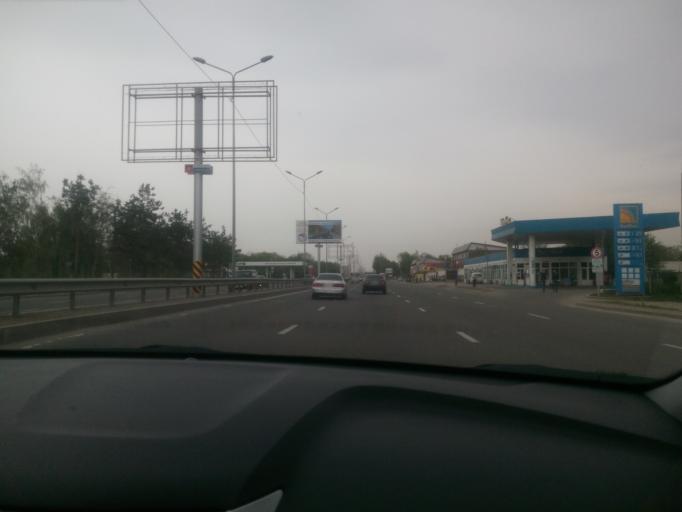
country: KZ
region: Almaty Qalasy
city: Almaty
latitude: 43.2367
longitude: 76.8061
